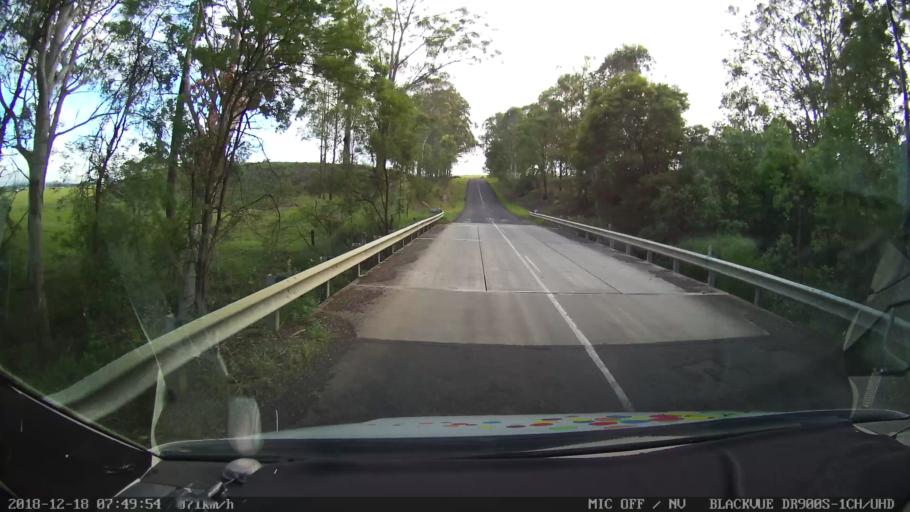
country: AU
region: New South Wales
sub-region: Kyogle
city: Kyogle
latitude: -28.4500
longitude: 152.5719
